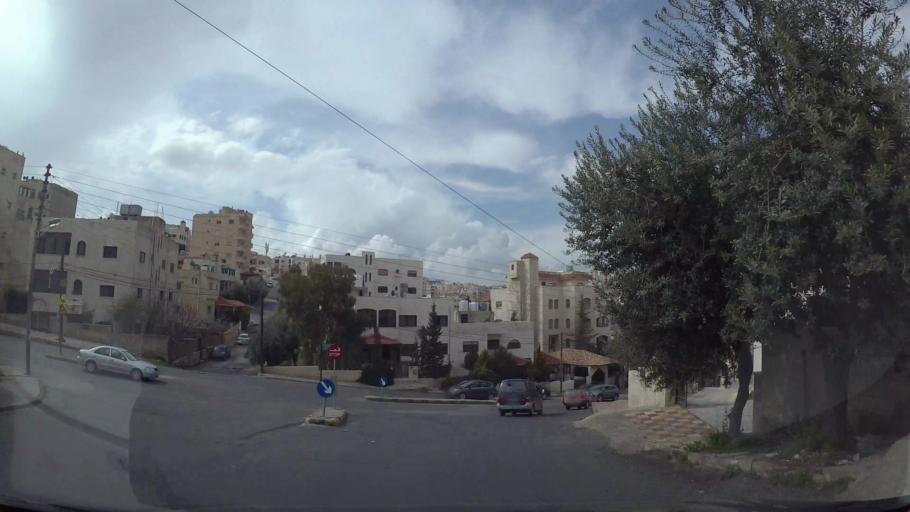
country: JO
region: Amman
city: Amman
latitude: 32.0051
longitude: 35.9398
